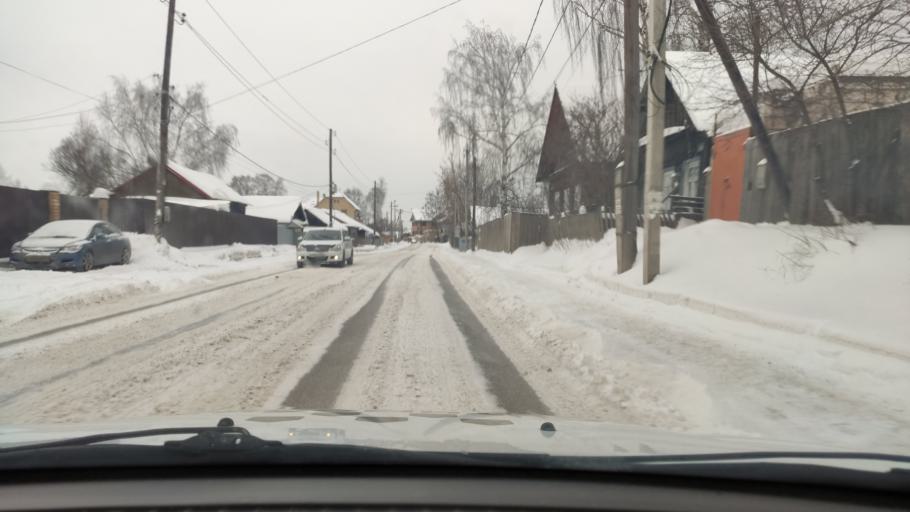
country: RU
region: Perm
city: Perm
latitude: 58.0343
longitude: 56.2463
